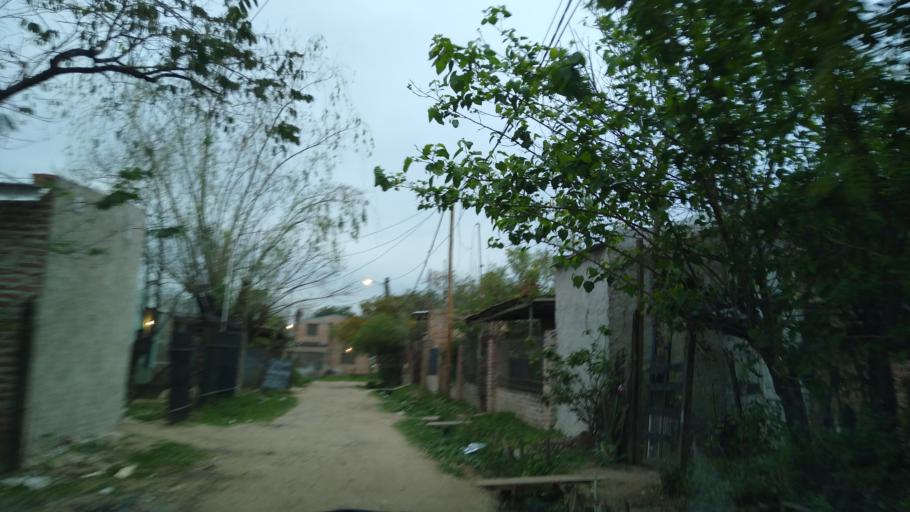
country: AR
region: Chaco
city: Resistencia
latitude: -27.4572
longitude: -58.9634
